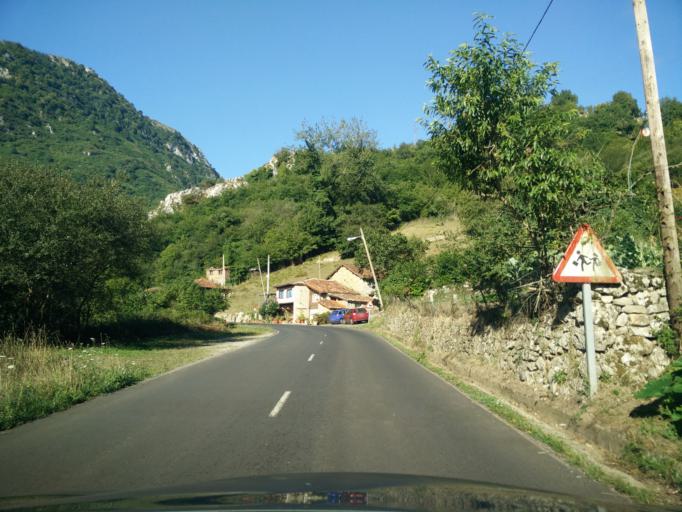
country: ES
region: Asturias
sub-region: Province of Asturias
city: Parres
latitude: 43.2595
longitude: -5.1993
